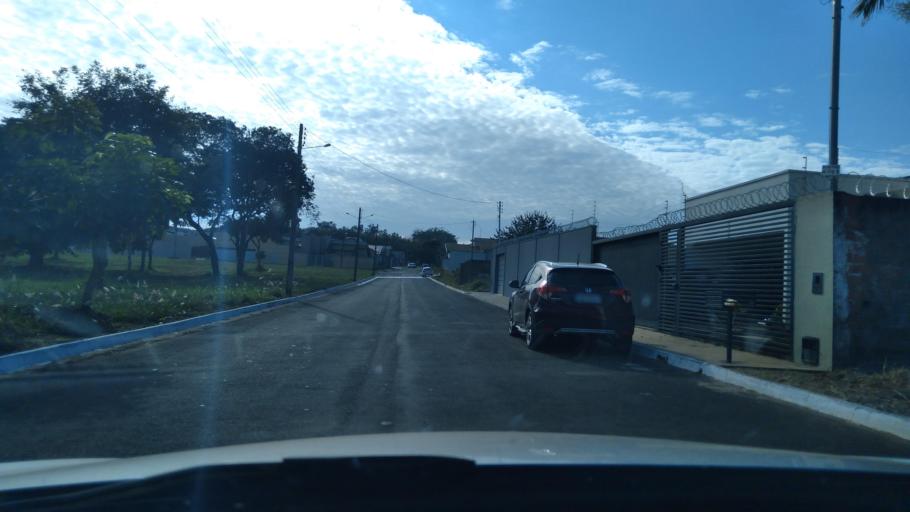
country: BR
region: Goias
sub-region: Mineiros
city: Mineiros
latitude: -17.5550
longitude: -52.5605
